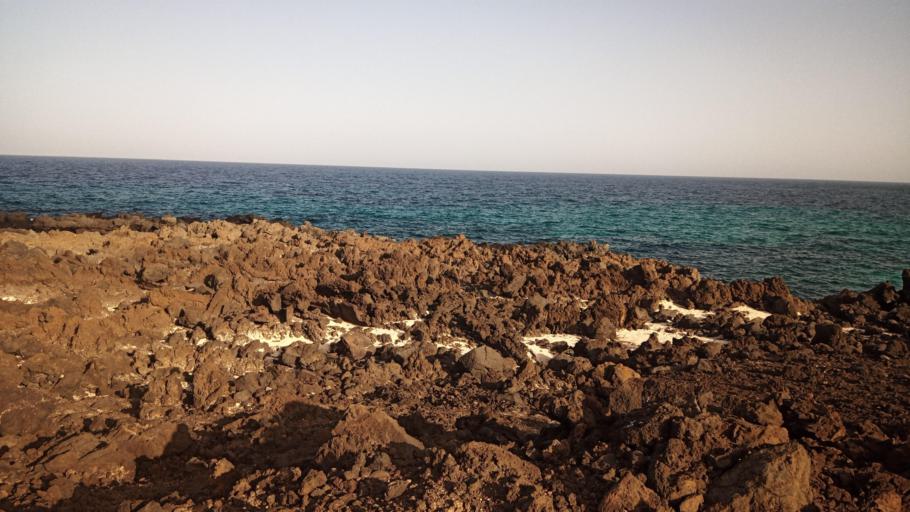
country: ES
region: Canary Islands
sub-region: Provincia de Las Palmas
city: Haria
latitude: 29.2072
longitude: -13.4241
